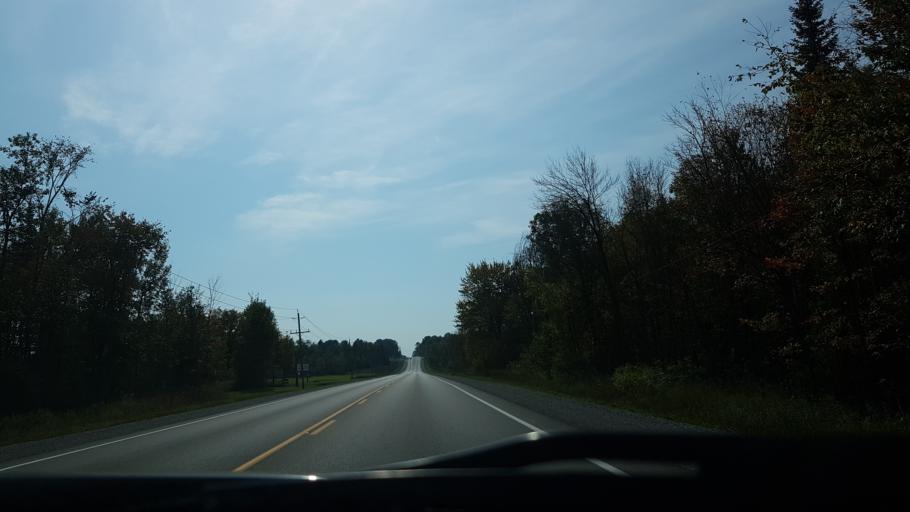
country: CA
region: Ontario
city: Orillia
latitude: 44.7338
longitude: -79.2901
